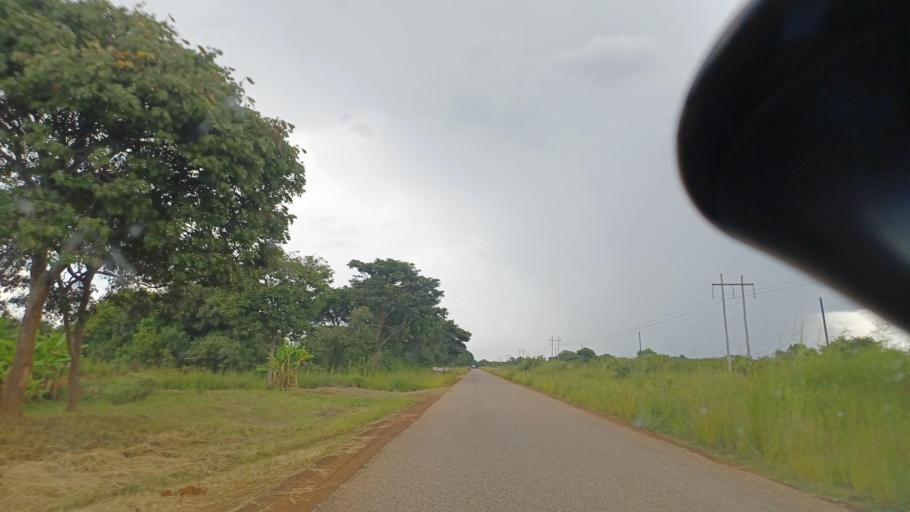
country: ZM
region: North-Western
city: Kasempa
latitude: -13.0376
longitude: 25.9945
